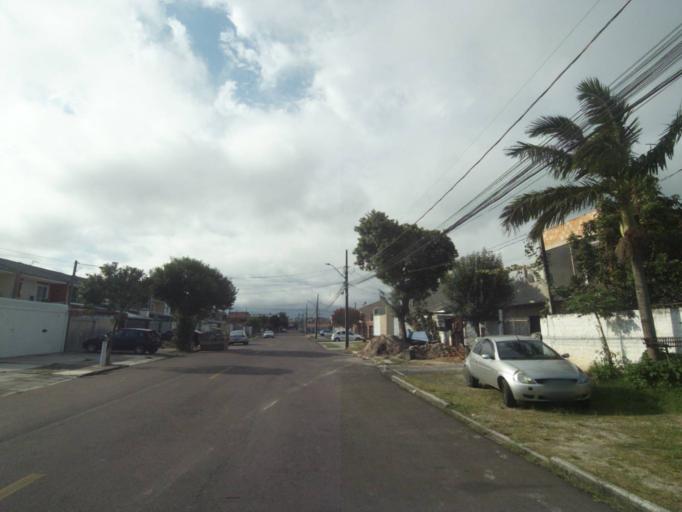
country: BR
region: Parana
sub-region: Pinhais
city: Pinhais
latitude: -25.4588
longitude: -49.2023
